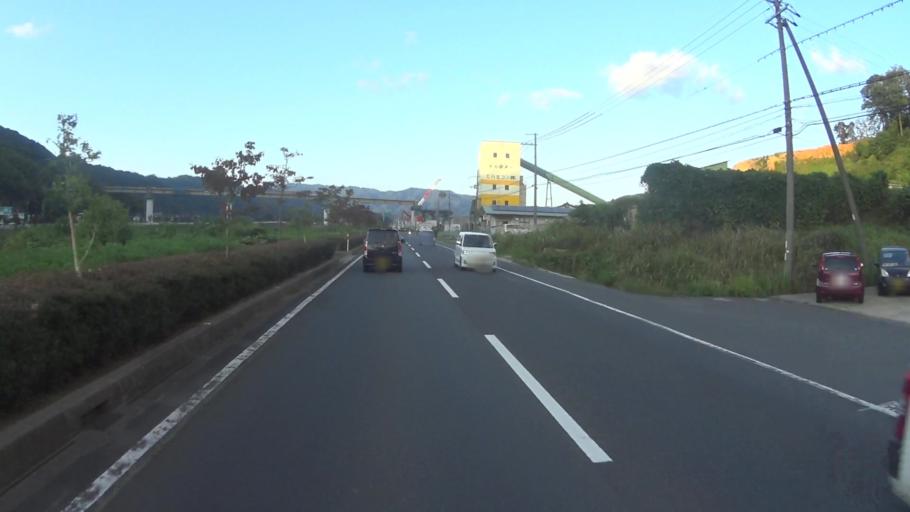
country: JP
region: Kyoto
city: Miyazu
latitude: 35.5477
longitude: 135.1361
